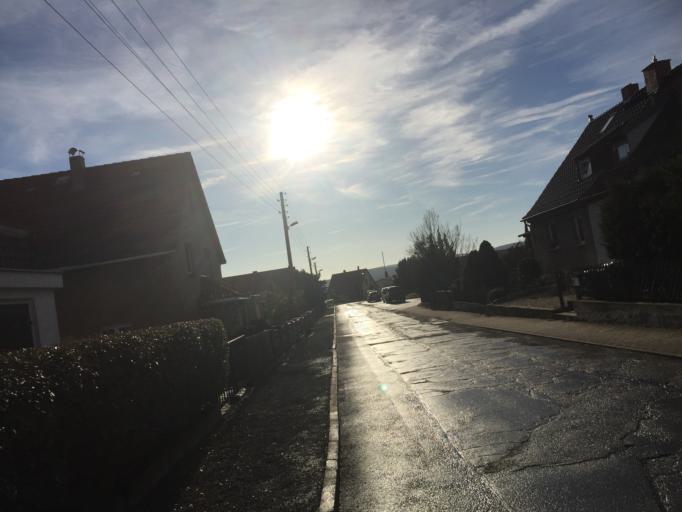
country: DE
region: Thuringia
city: Orlamunde
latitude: 50.7720
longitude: 11.5148
